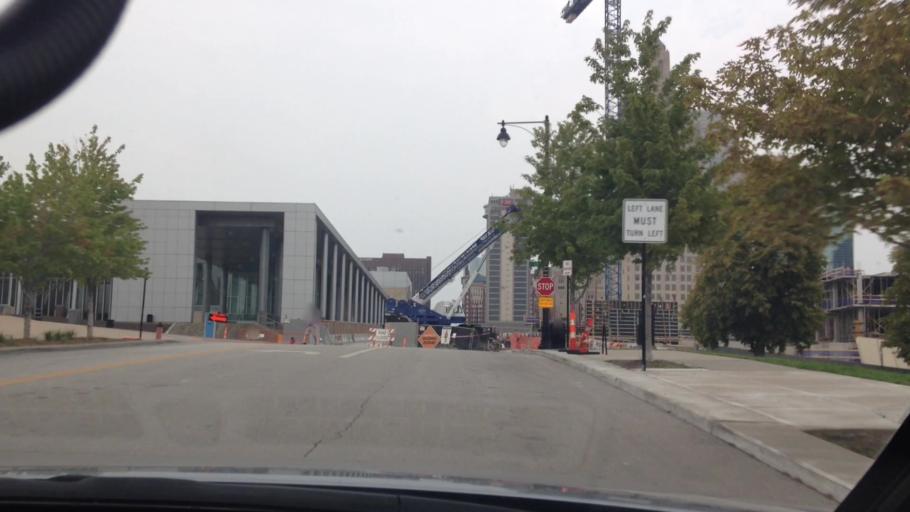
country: US
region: Missouri
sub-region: Jackson County
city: Kansas City
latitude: 39.0941
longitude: -94.5858
